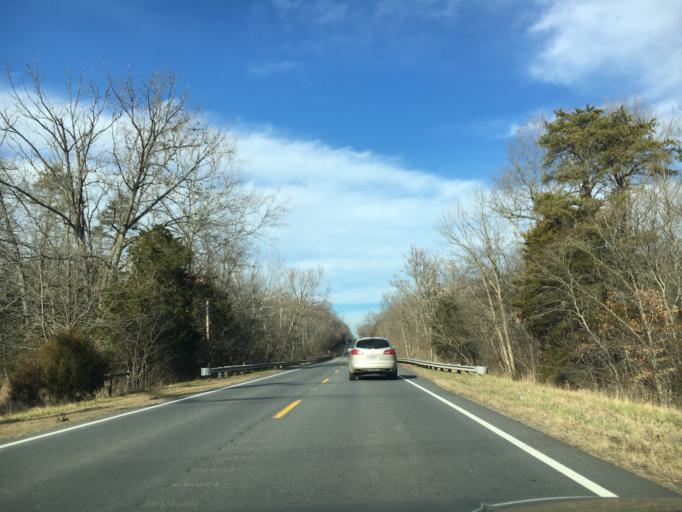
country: US
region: Virginia
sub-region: Culpeper County
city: Culpeper
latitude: 38.3626
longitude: -77.9750
